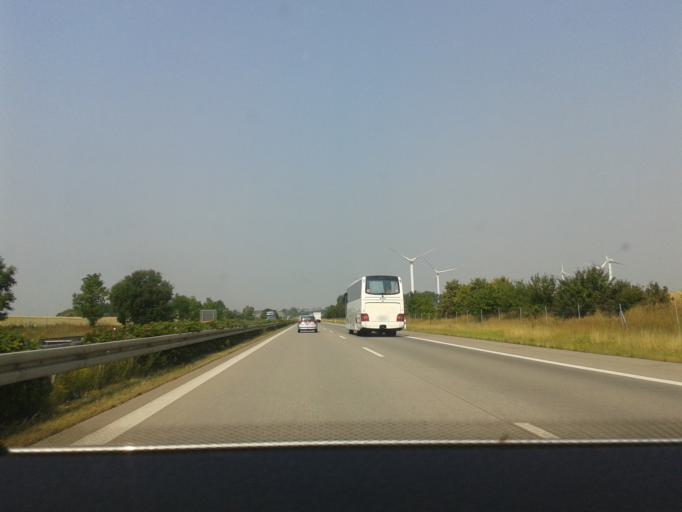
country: DE
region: Saxony
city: Bockelwitz
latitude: 51.1908
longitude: 12.9999
